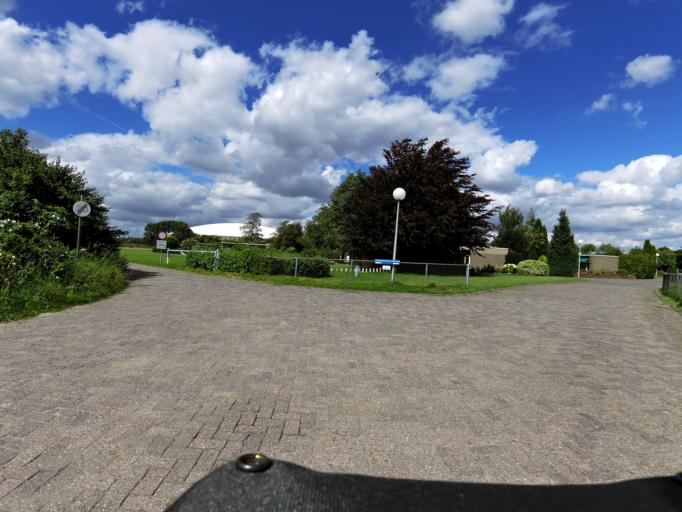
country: NL
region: South Holland
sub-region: Gemeente Oud-Beijerland
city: Oud-Beijerland
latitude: 51.8319
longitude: 4.3956
